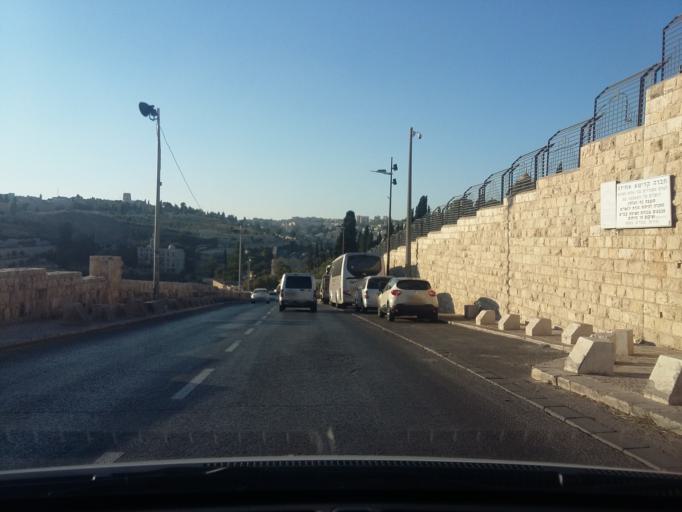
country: PS
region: West Bank
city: Old City
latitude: 31.7762
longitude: 35.2403
